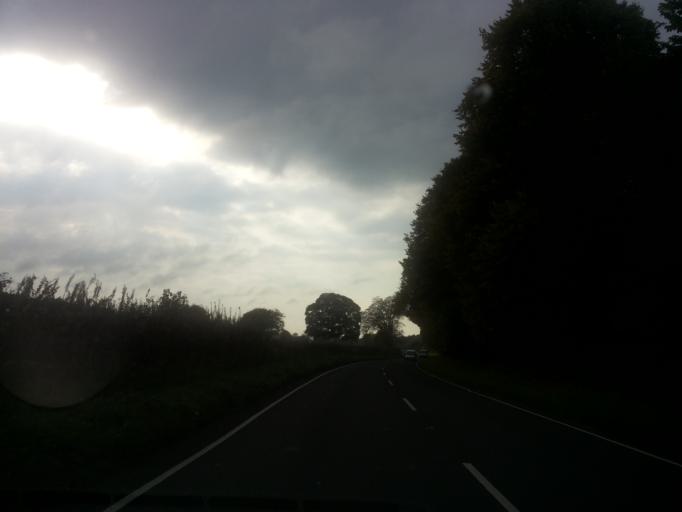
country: GB
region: England
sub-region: Buckinghamshire
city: Great Missenden
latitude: 51.7316
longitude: -0.7276
